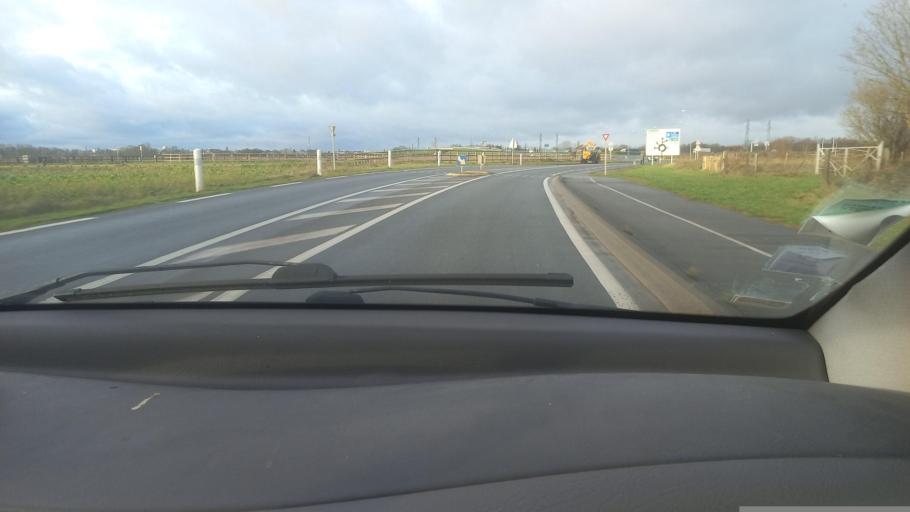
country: FR
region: Centre
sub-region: Departement de l'Indre
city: Deols
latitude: 46.8214
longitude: 1.7417
